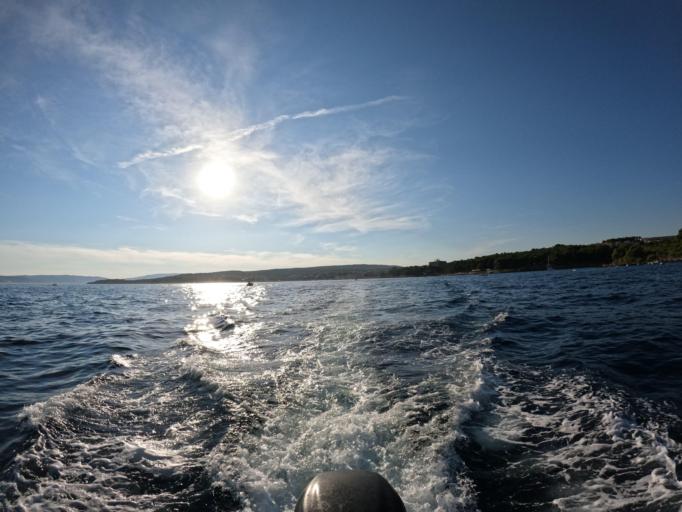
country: HR
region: Primorsko-Goranska
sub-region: Grad Krk
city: Krk
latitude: 45.0207
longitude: 14.5894
